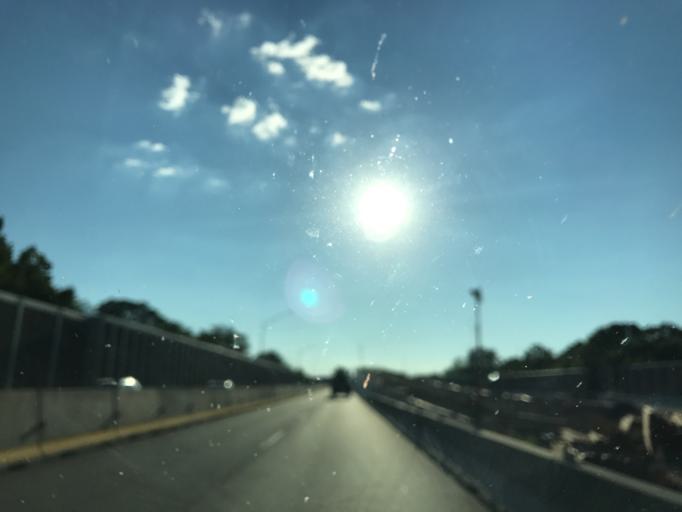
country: US
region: Pennsylvania
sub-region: Bucks County
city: Bristol
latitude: 40.1264
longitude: -74.8737
